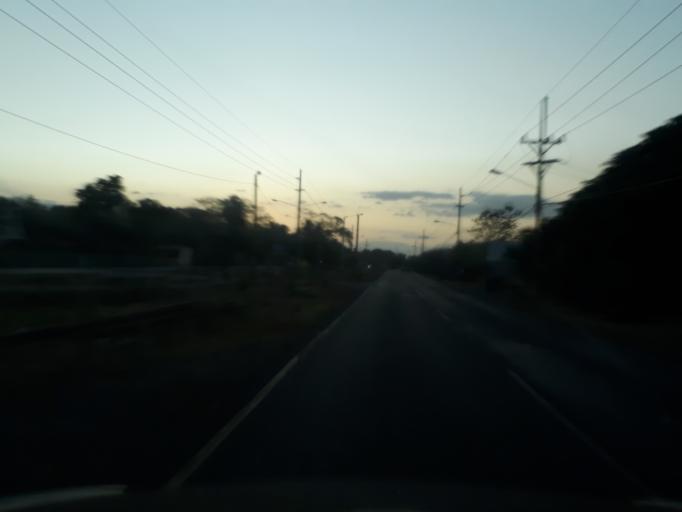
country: CR
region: Puntarenas
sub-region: Canton Central de Puntarenas
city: Chacarita
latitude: 9.9783
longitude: -84.7603
